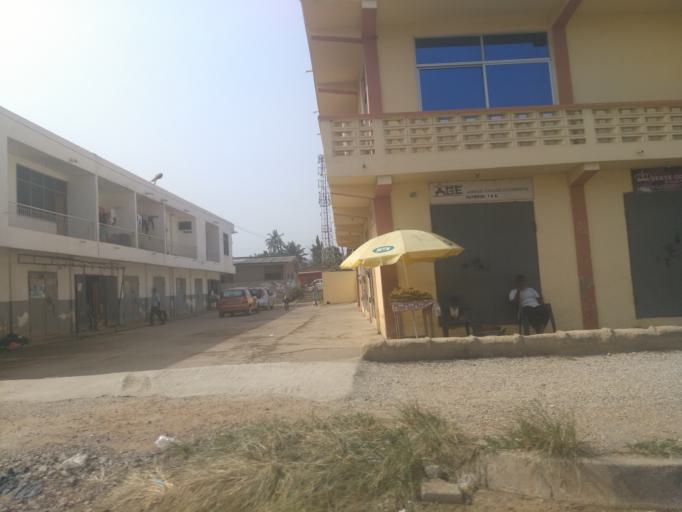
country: GH
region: Greater Accra
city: Gbawe
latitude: 5.5772
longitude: -0.2563
